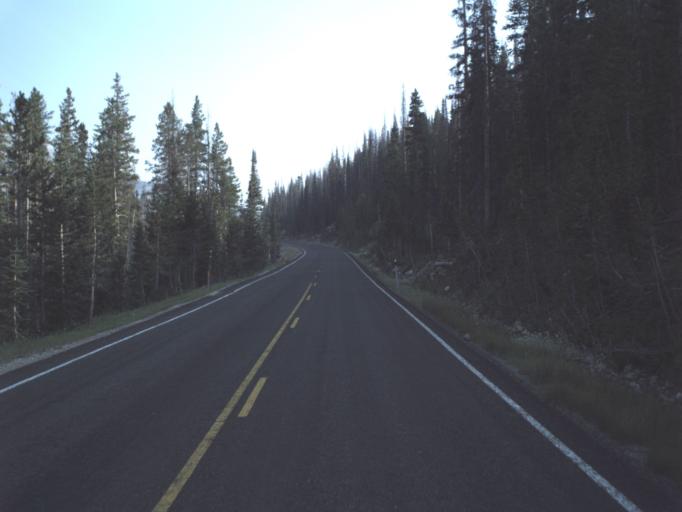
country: US
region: Utah
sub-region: Summit County
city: Kamas
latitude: 40.7499
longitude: -110.8760
